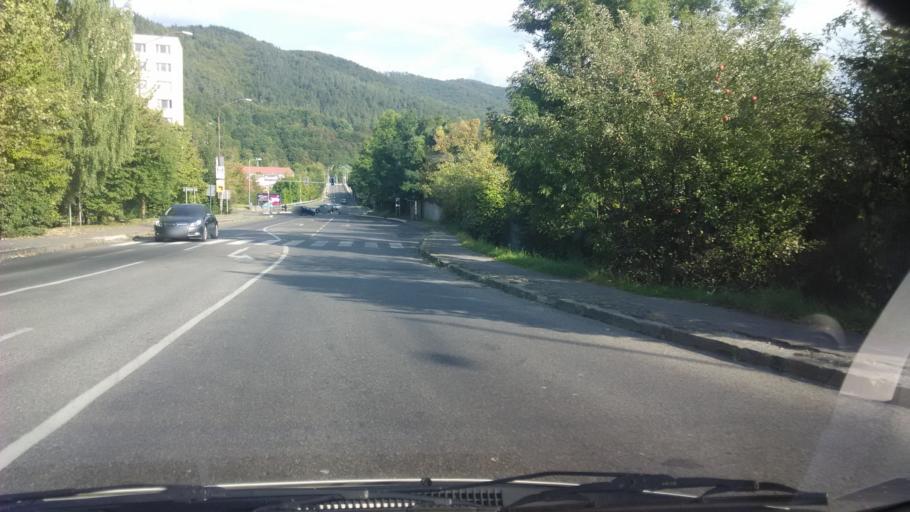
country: SK
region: Banskobystricky
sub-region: Okres Banska Bystrica
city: Banska Bystrica
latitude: 48.7169
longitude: 19.1326
